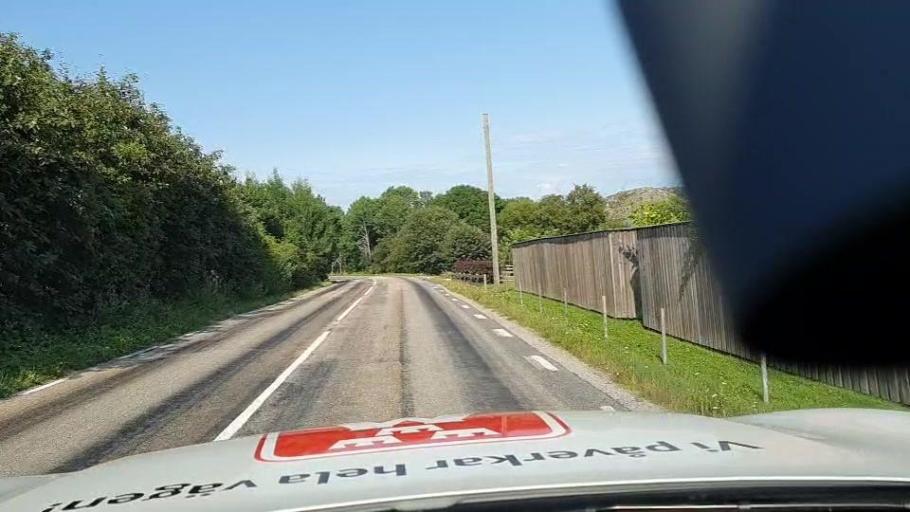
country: SE
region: Vaestra Goetaland
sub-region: Tjorns Kommun
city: Skaerhamn
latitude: 58.0831
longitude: 11.4851
